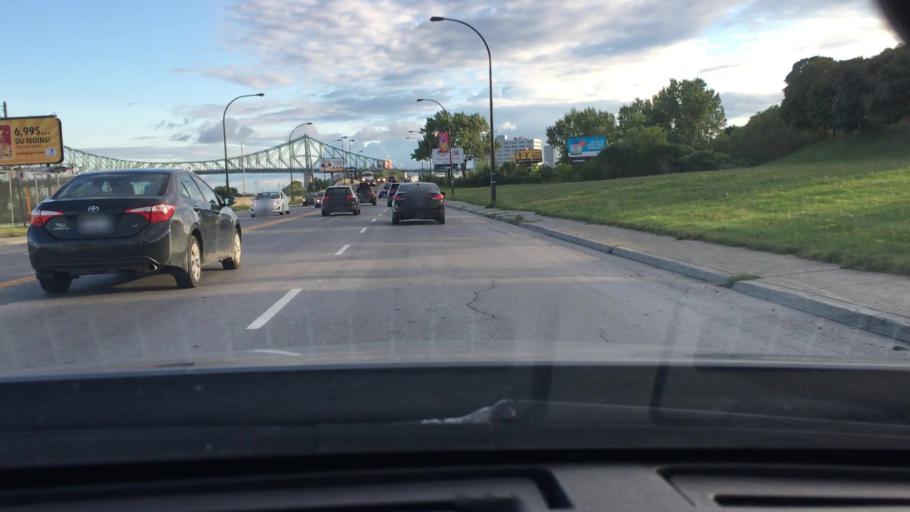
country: CA
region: Quebec
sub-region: Monteregie
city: Longueuil
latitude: 45.5337
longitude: -73.5426
